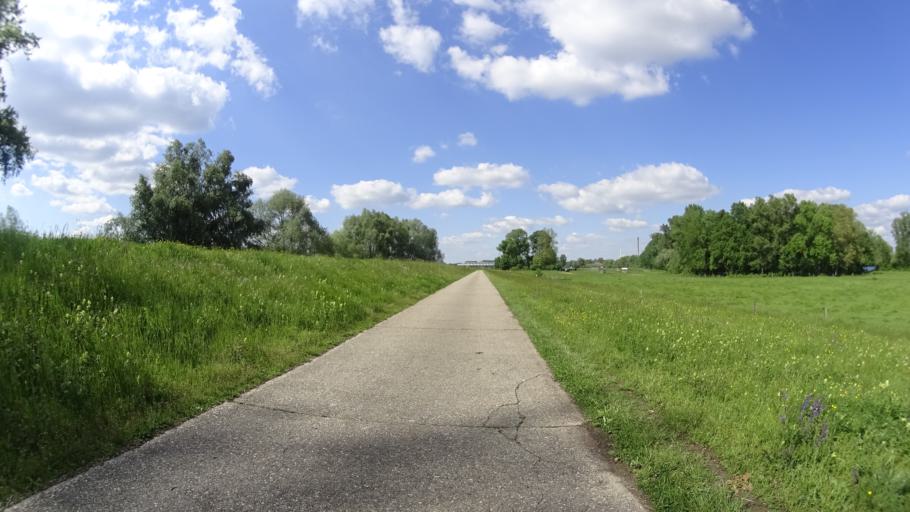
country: DE
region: Rheinland-Pfalz
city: Worth am Rhein
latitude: 49.0234
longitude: 8.3035
